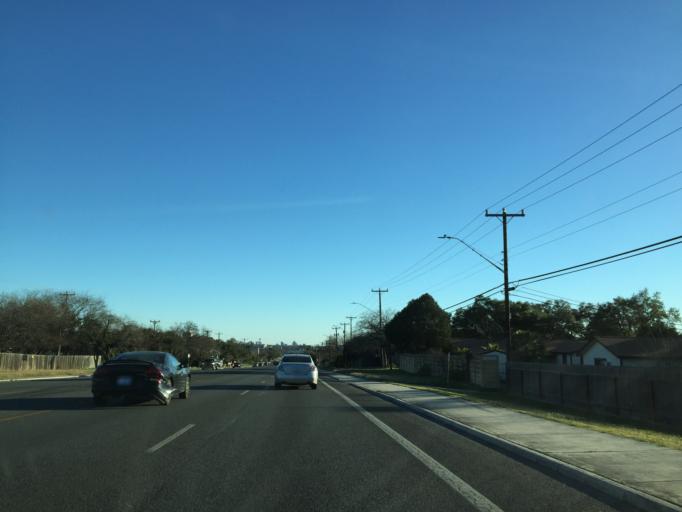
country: US
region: Texas
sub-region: Bexar County
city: Castle Hills
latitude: 29.5325
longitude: -98.5061
